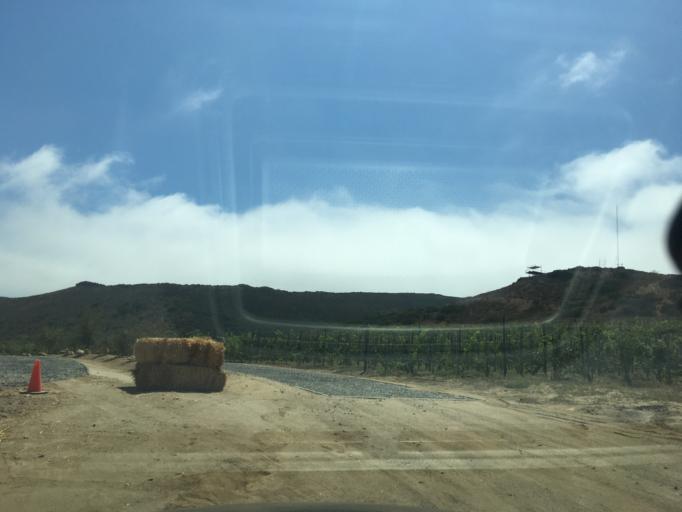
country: MX
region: Baja California
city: El Sauzal
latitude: 31.9462
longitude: -116.7372
